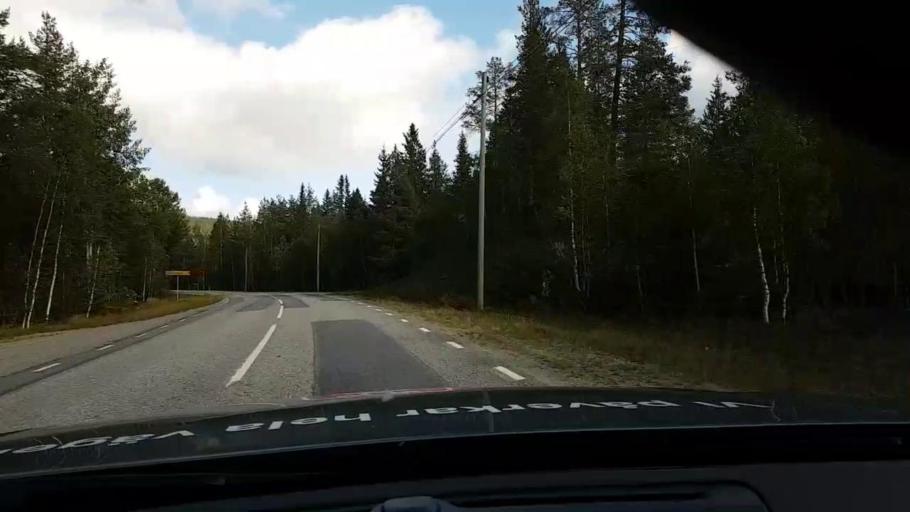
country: SE
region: Vaesterbotten
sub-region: Asele Kommun
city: Asele
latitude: 63.7884
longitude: 17.5958
